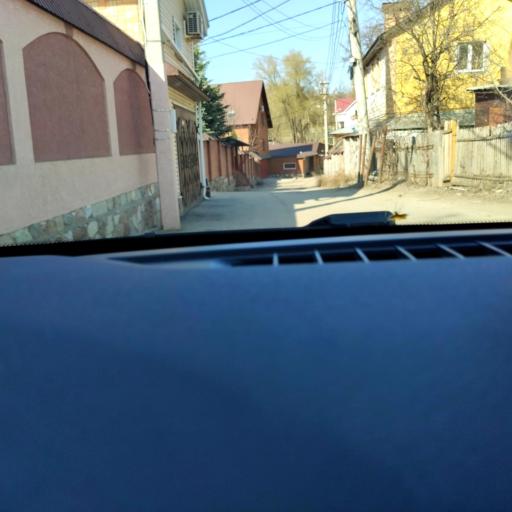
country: RU
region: Samara
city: Samara
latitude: 53.2739
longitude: 50.2163
